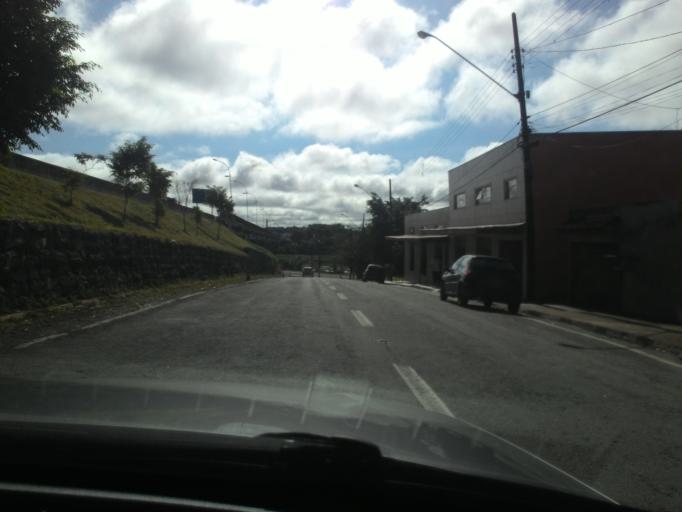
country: BR
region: Sao Paulo
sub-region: Registro
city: Registro
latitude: -24.4915
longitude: -47.8361
